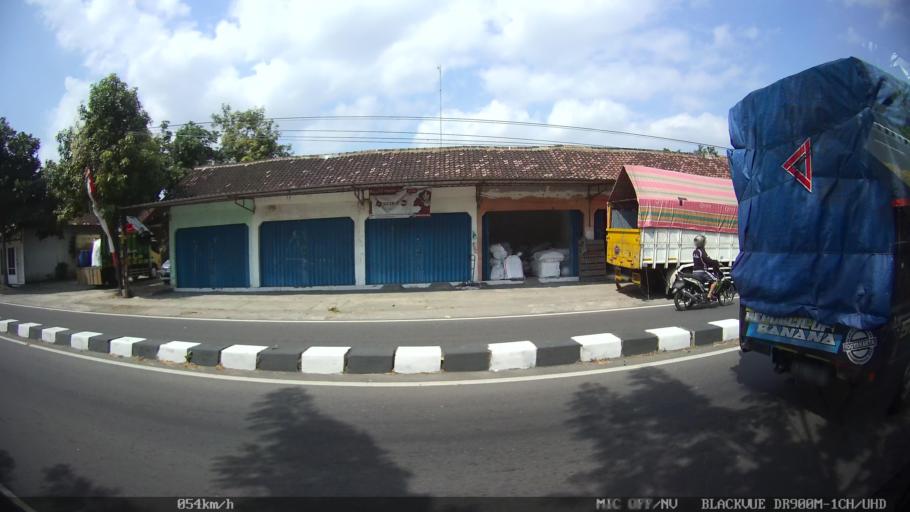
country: ID
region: Daerah Istimewa Yogyakarta
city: Kasihan
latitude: -7.8264
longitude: 110.3432
